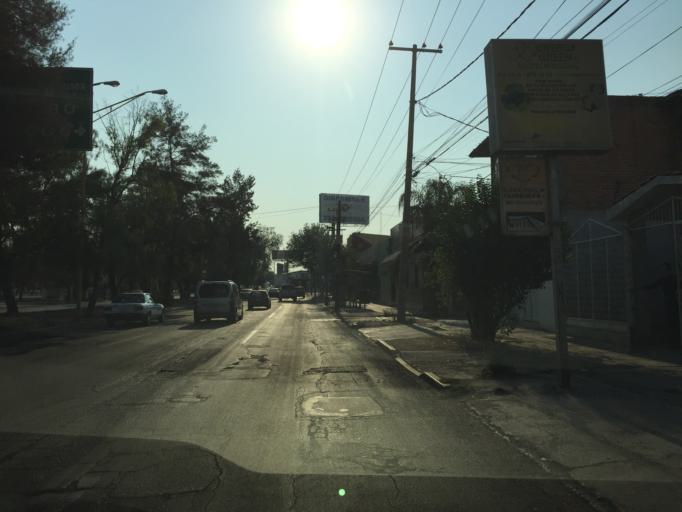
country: MX
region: Aguascalientes
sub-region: Aguascalientes
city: Aguascalientes
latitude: 21.8593
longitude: -102.3030
